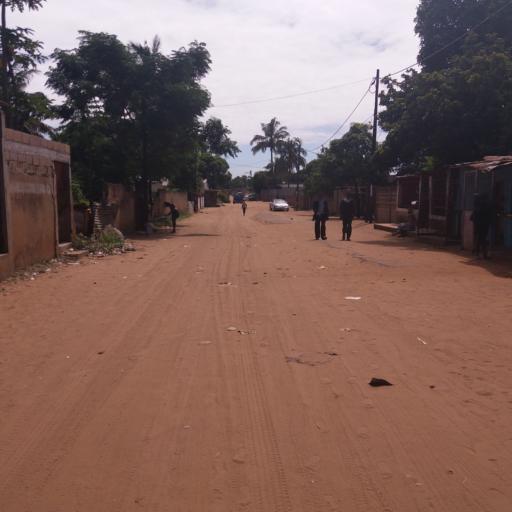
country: MZ
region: Maputo City
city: Maputo
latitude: -25.9118
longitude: 32.5903
